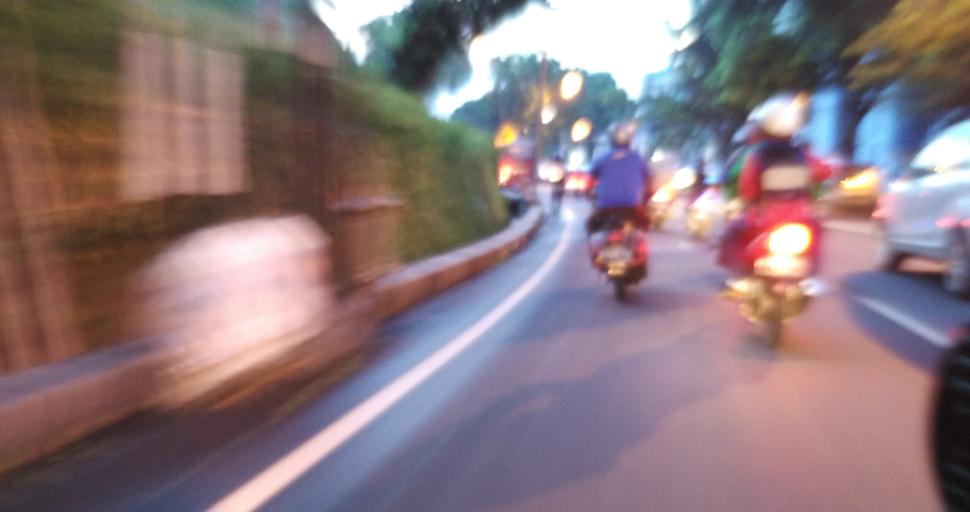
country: ID
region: Central Java
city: Semarang
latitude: -7.0130
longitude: 110.4174
